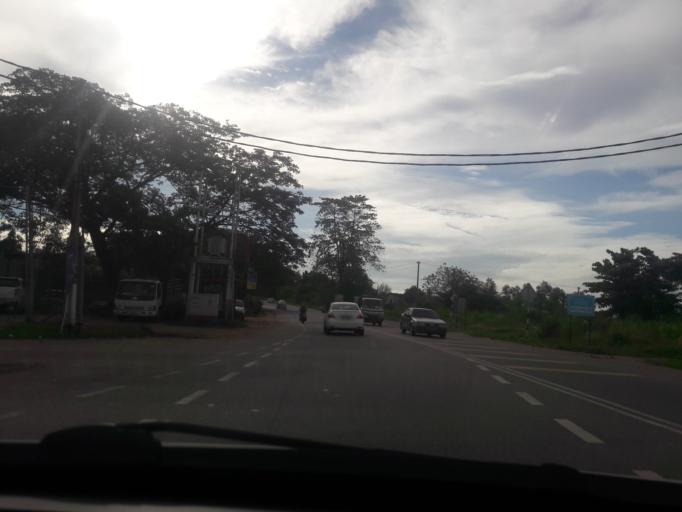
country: MY
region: Kedah
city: Sungai Petani
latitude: 5.6352
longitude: 100.5137
